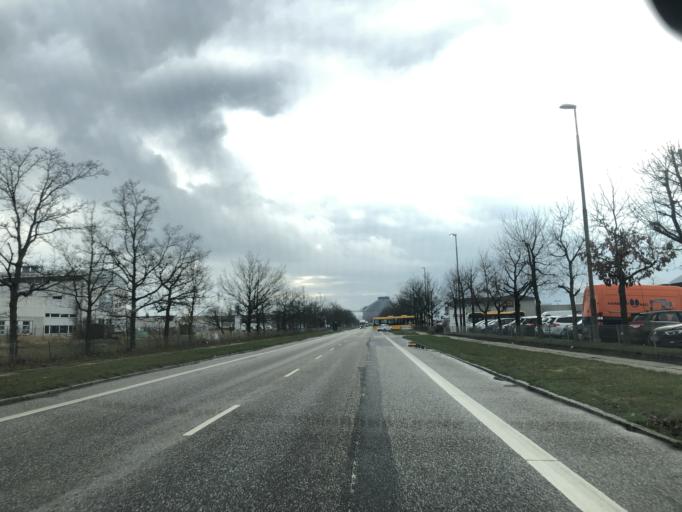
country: DK
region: Capital Region
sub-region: Hvidovre Kommune
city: Hvidovre
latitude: 55.6108
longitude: 12.4901
